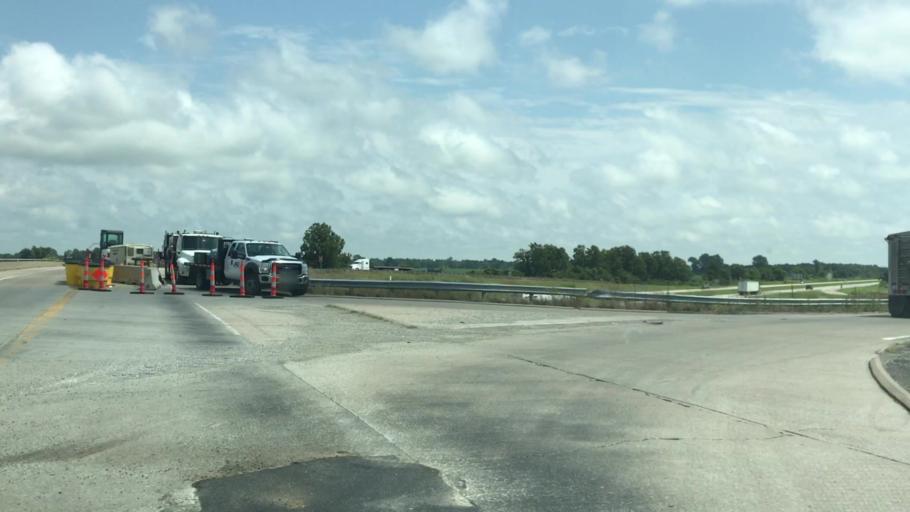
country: US
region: Missouri
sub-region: Pemiscot County
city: Caruthersville
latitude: 36.1762
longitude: -89.6945
